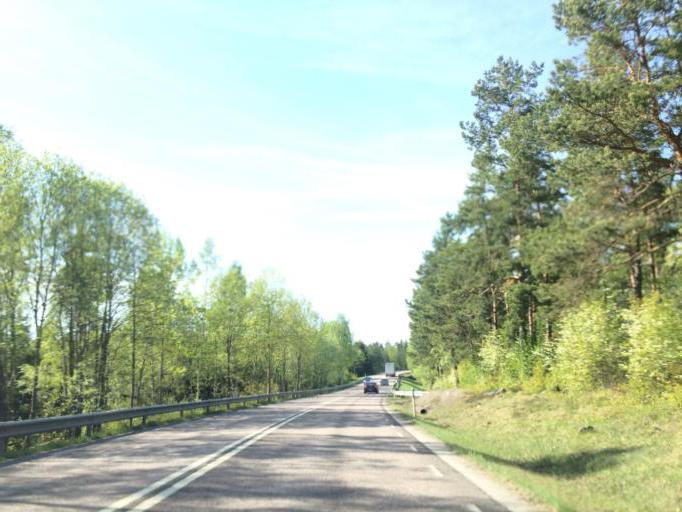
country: SE
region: Soedermanland
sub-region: Katrineholms Kommun
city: Katrineholm
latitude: 59.1397
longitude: 16.1241
